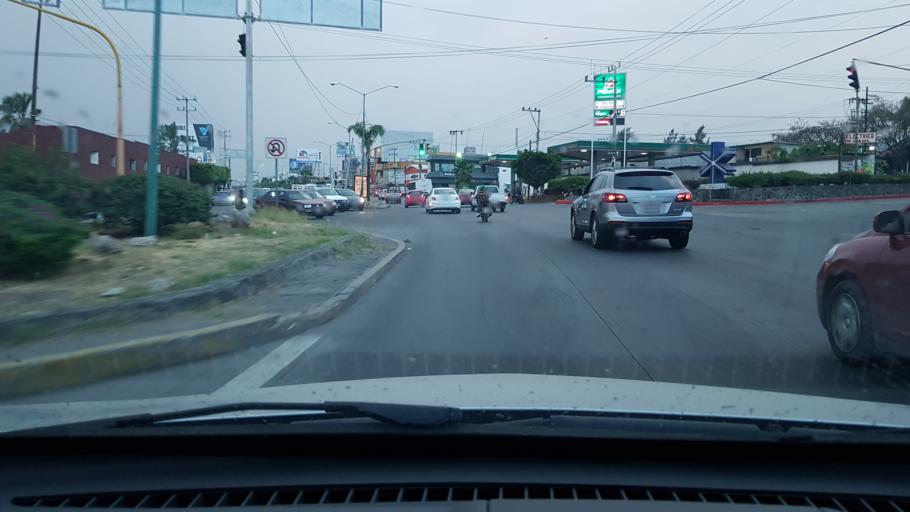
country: MX
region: Morelos
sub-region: Tepoztlan
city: Loma Bonita
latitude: 18.9107
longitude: -99.1810
